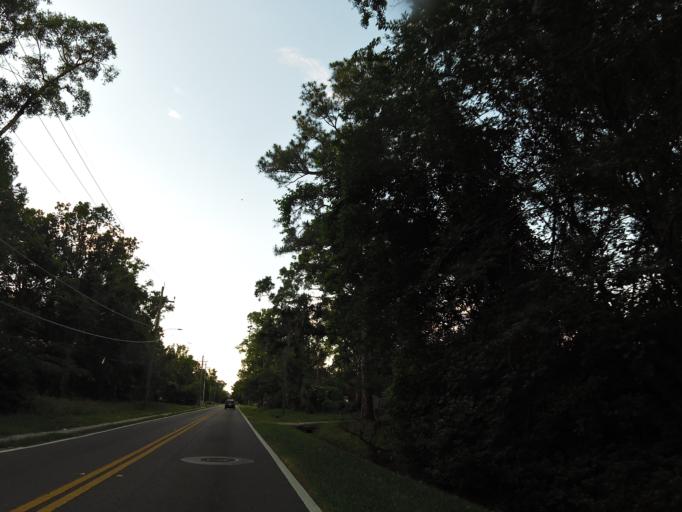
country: US
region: Florida
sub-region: Duval County
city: Jacksonville
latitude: 30.2955
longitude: -81.7390
